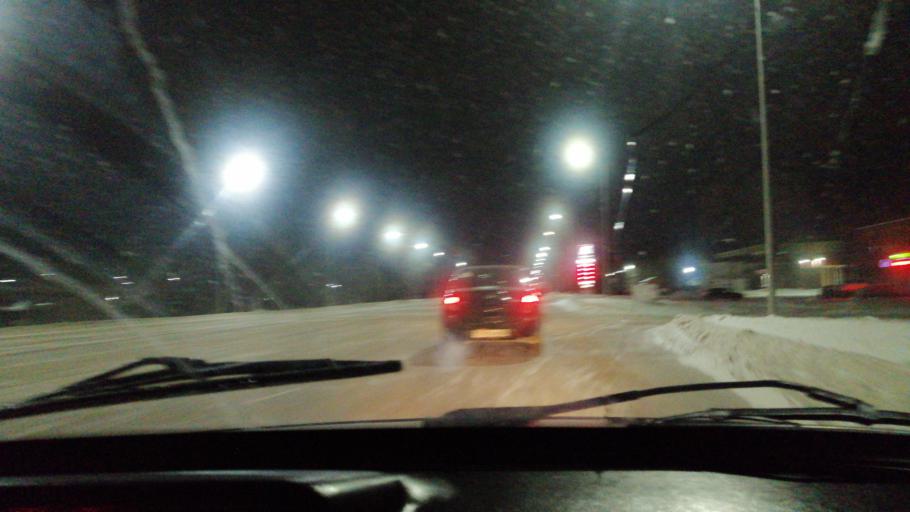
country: KZ
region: Aqtoebe
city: Aqtobe
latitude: 50.2969
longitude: 57.1871
